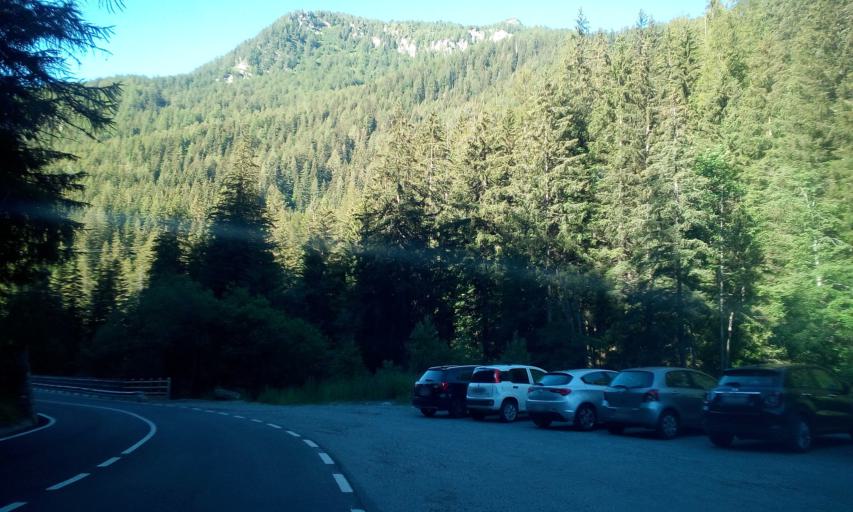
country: IT
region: Aosta Valley
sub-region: Valle d'Aosta
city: Ayas
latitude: 45.8593
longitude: 7.7307
